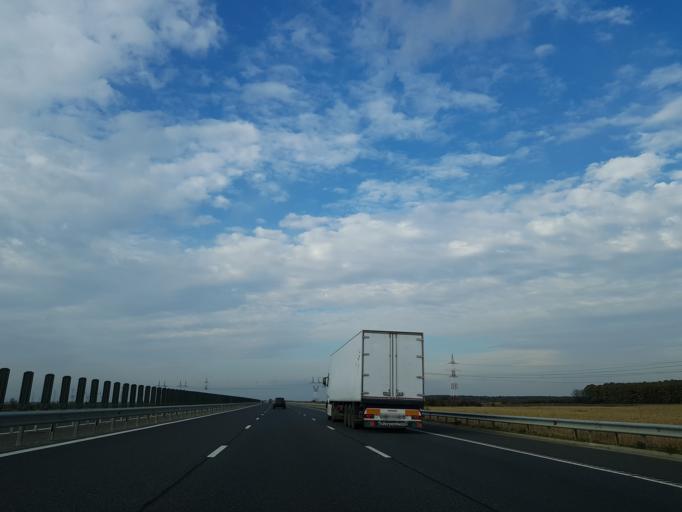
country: RO
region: Ilfov
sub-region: Comuna Tunari
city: Tunari
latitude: 44.5734
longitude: 26.1806
